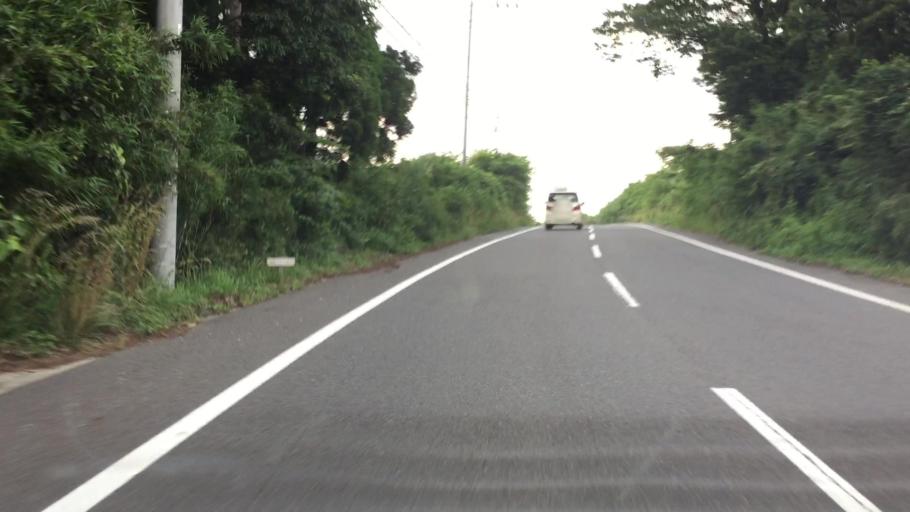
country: JP
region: Tochigi
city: Kuroiso
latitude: 37.0791
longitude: 140.0511
